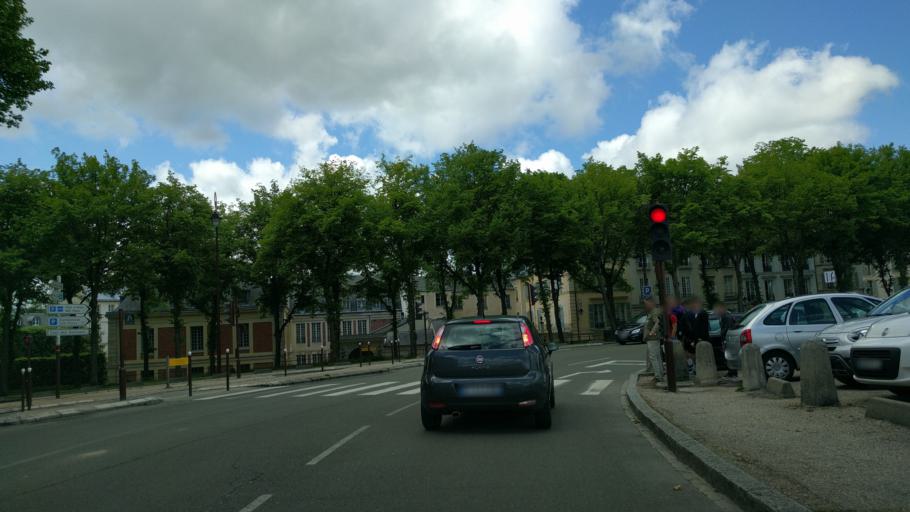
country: FR
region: Ile-de-France
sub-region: Departement des Yvelines
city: Versailles
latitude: 48.8022
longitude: 2.1255
